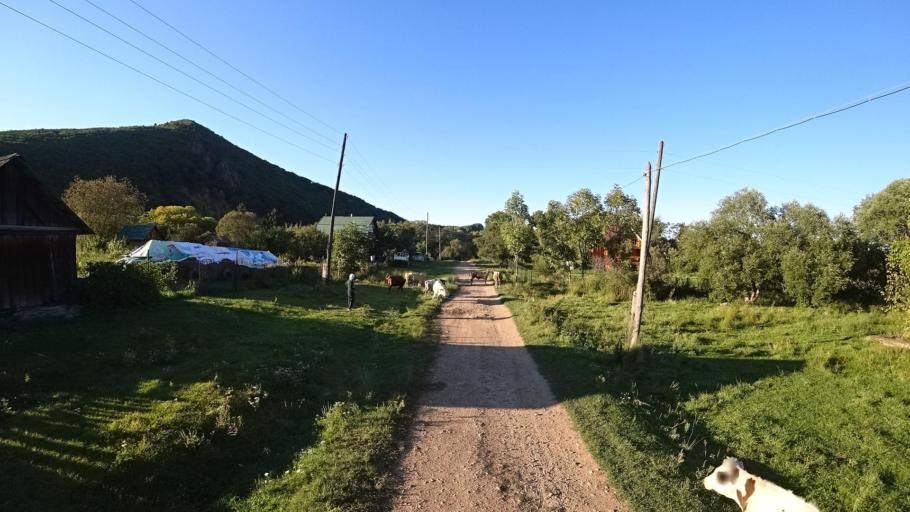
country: RU
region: Primorskiy
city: Kirovskiy
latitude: 44.8339
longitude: 133.5757
